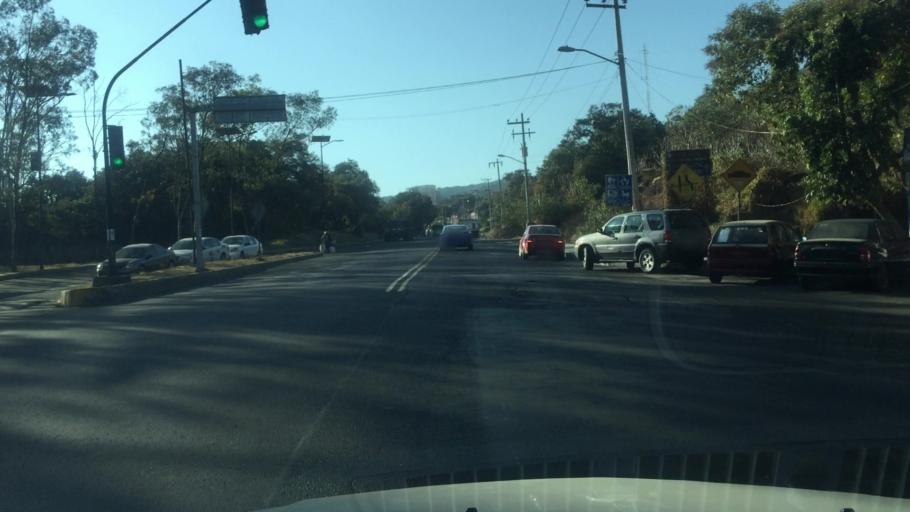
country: MX
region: Mexico City
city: Tlalpan
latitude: 19.2713
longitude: -99.2058
